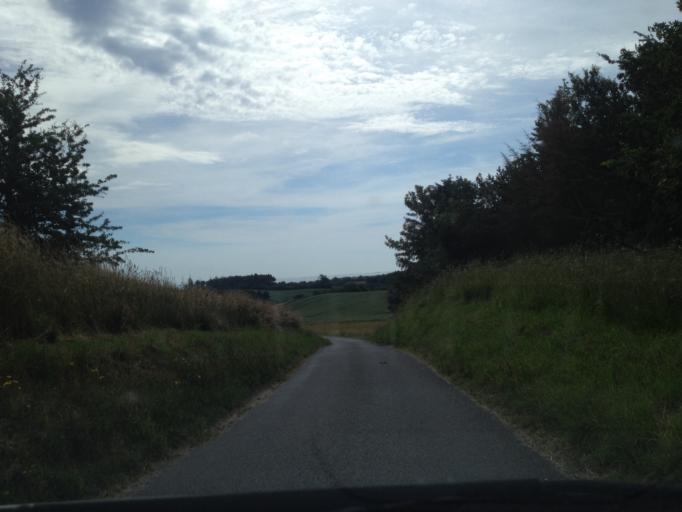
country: DK
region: Central Jutland
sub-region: Samso Kommune
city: Tranebjerg
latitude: 55.9694
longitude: 10.5306
